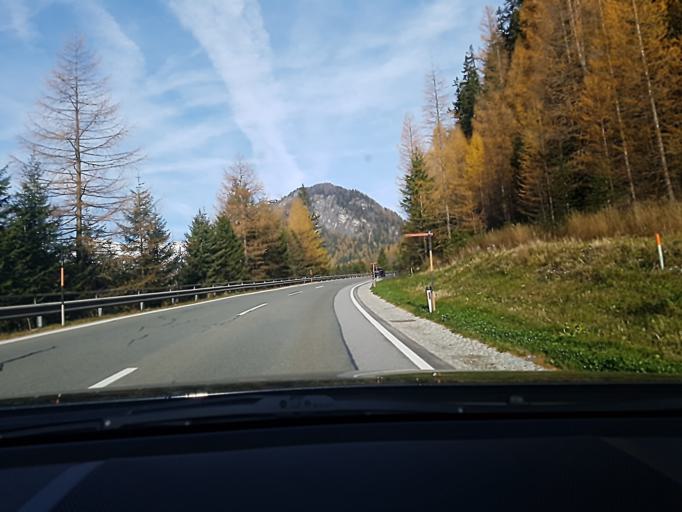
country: AT
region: Salzburg
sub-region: Politischer Bezirk Tamsweg
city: Tweng
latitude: 47.1953
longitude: 13.5935
